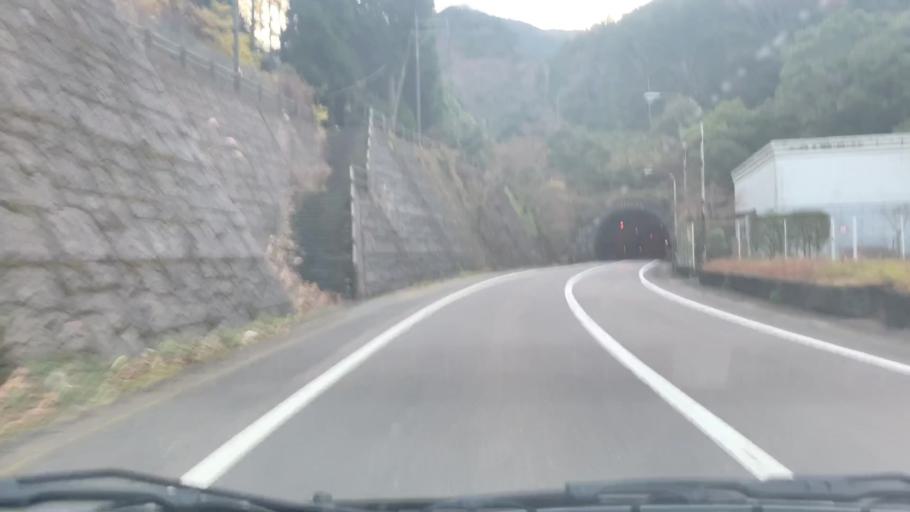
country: JP
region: Saga Prefecture
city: Kashima
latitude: 32.9986
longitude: 130.0623
